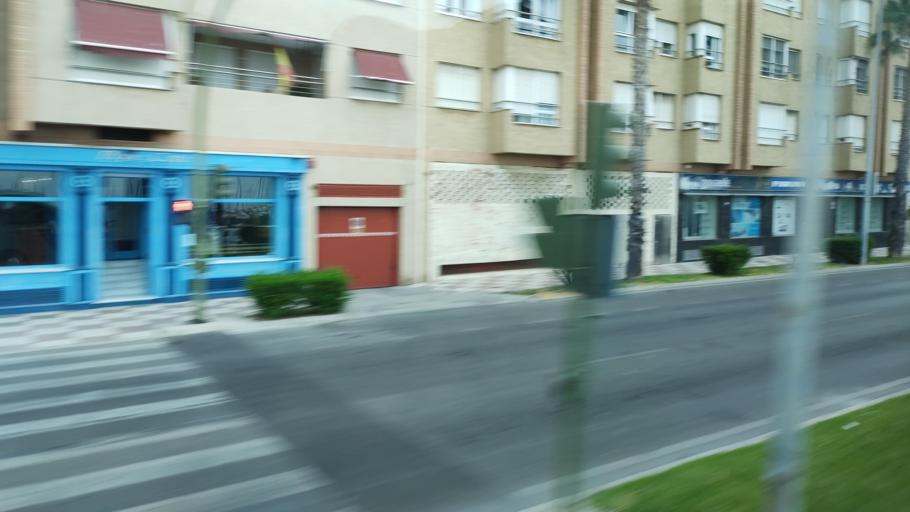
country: ES
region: Andalusia
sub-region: Provincia de Cadiz
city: La Linea de la Concepcion
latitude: 36.1617
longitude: -5.3564
